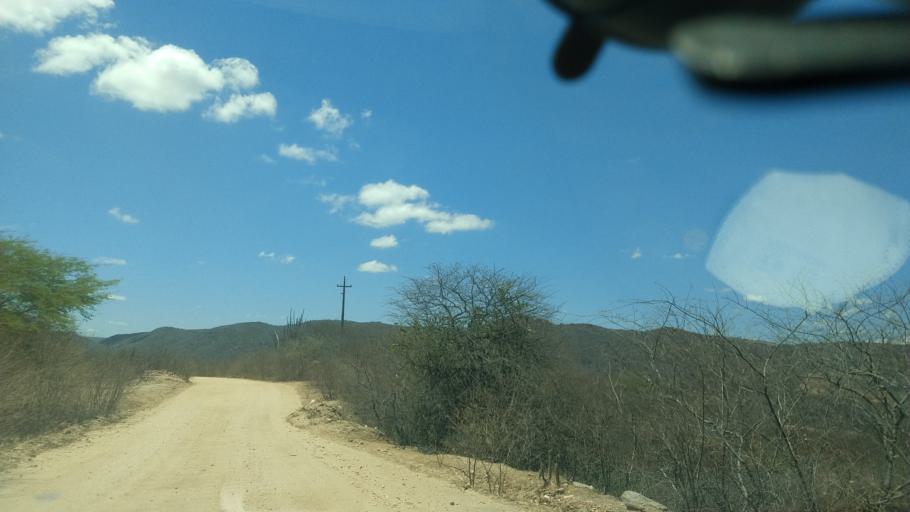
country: BR
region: Rio Grande do Norte
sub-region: Cerro Cora
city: Cerro Cora
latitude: -6.0146
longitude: -36.3046
